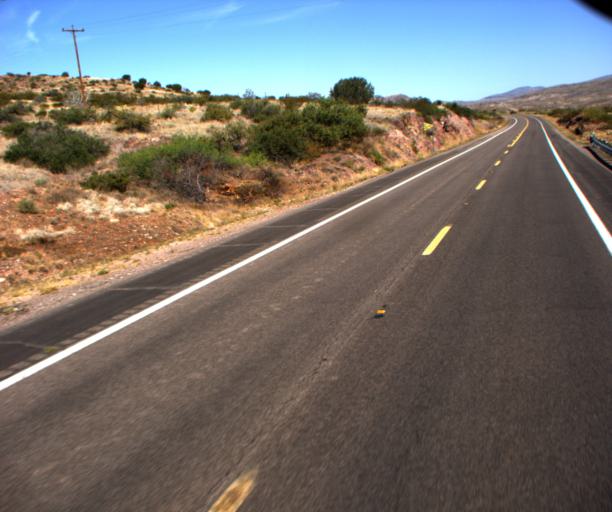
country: US
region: Arizona
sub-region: Greenlee County
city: Clifton
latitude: 32.7566
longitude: -109.2423
